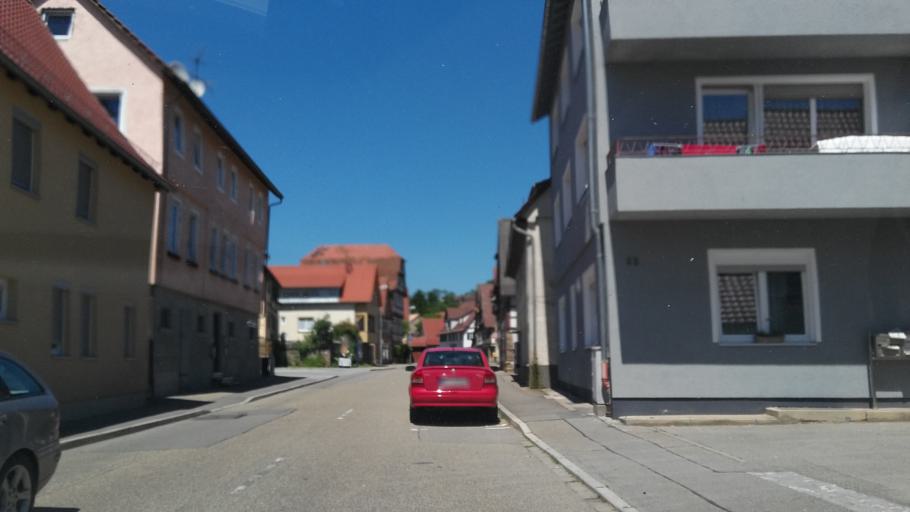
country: DE
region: Baden-Wuerttemberg
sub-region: Karlsruhe Region
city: Muhlacker
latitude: 48.9759
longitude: 8.8617
